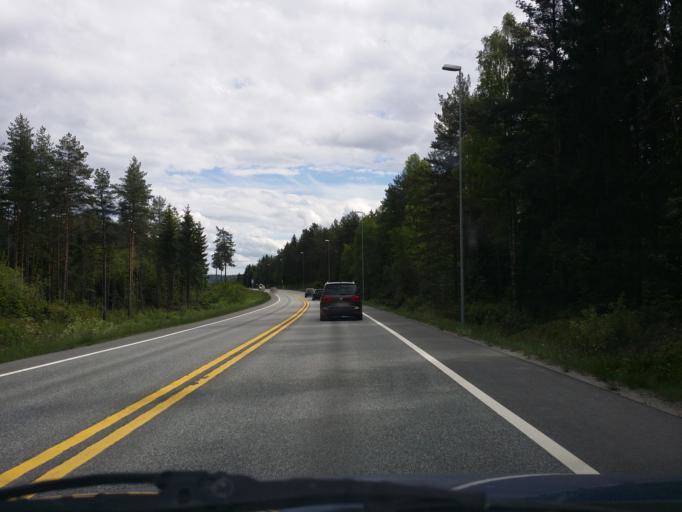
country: NO
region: Hedmark
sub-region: Stange
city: Stange
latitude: 60.7106
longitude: 11.2528
